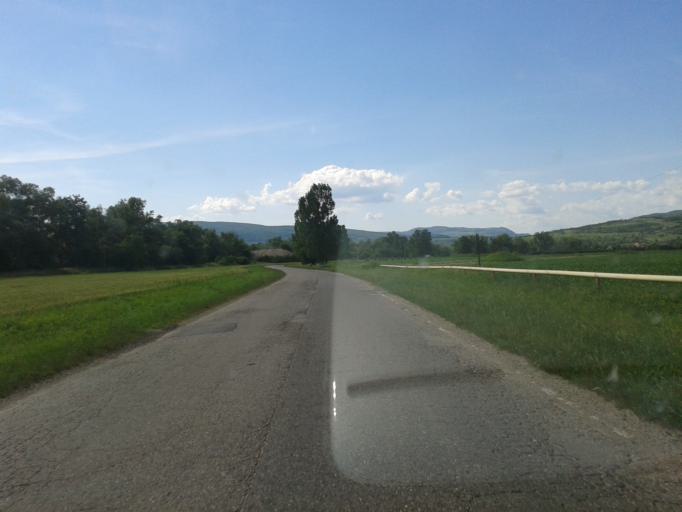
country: RO
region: Hunedoara
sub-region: Comuna Geoagiu
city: Geoagiu
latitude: 45.8914
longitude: 23.2314
